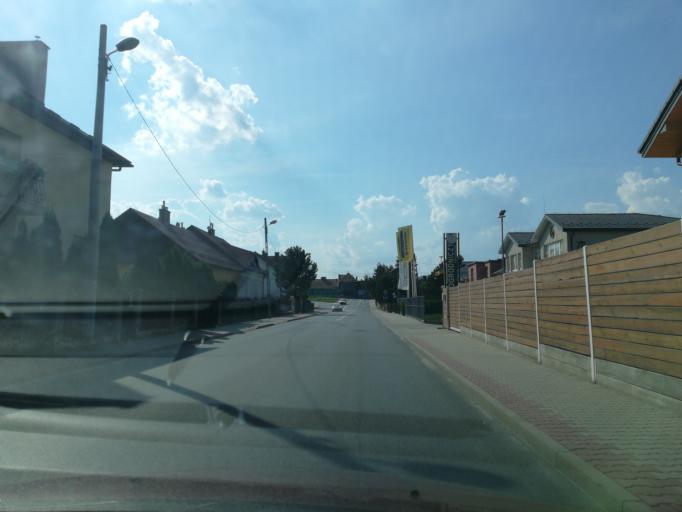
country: PL
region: Lesser Poland Voivodeship
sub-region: Powiat nowosadecki
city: Nowy Sacz
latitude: 49.6308
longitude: 20.6939
